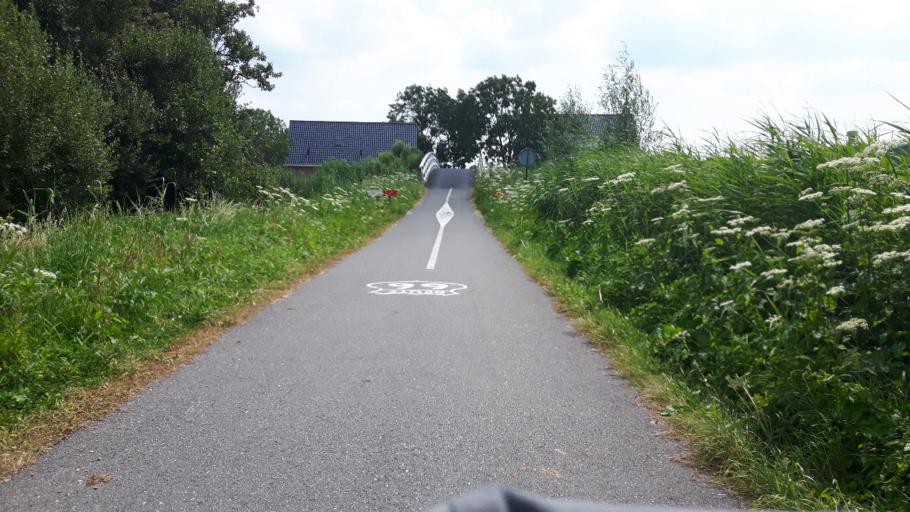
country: NL
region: South Holland
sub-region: Gemeente Giessenlanden
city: Giessenburg
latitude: 51.9010
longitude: 4.8858
